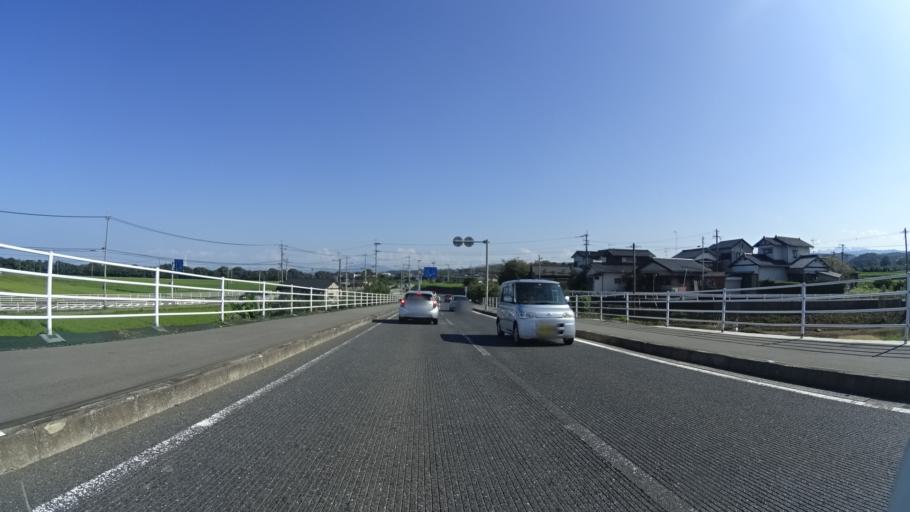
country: JP
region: Fukuoka
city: Shiida
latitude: 33.6451
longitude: 131.0671
